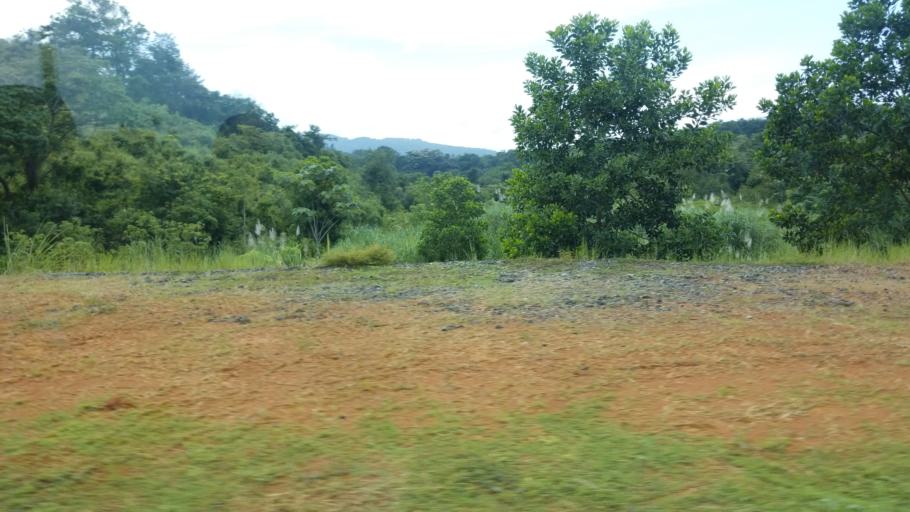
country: PA
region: Panama
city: Las Cumbres
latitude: 9.1101
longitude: -79.4761
